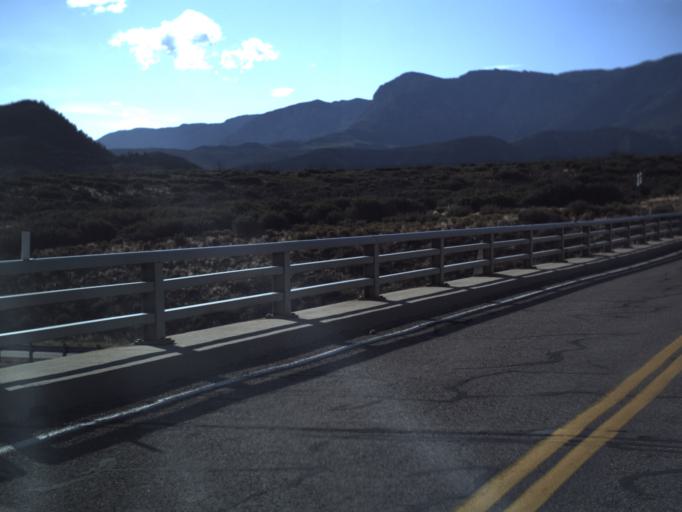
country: US
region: Utah
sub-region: Washington County
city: Toquerville
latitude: 37.3260
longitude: -113.2849
